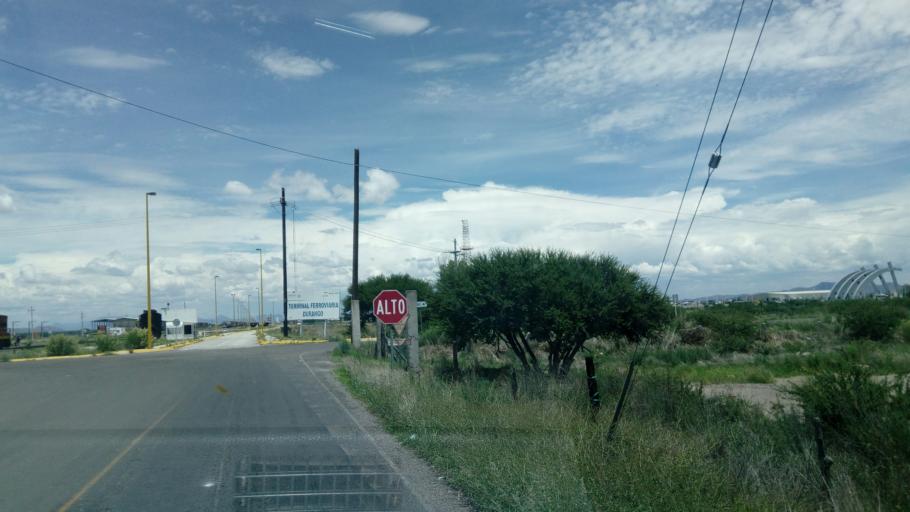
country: MX
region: Durango
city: Victoria de Durango
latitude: 24.1595
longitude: -104.5210
